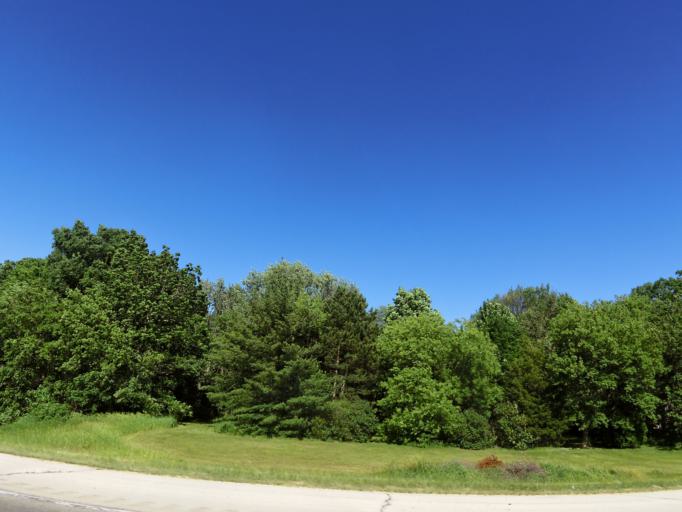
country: US
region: Illinois
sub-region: Winnebago County
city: Roscoe
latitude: 42.4093
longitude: -89.0120
